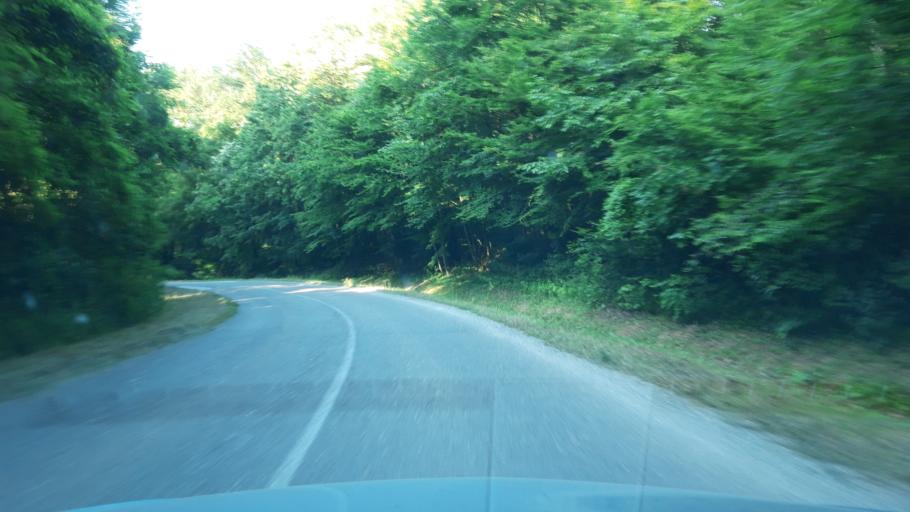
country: RS
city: Glozan
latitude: 45.1539
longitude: 19.5859
